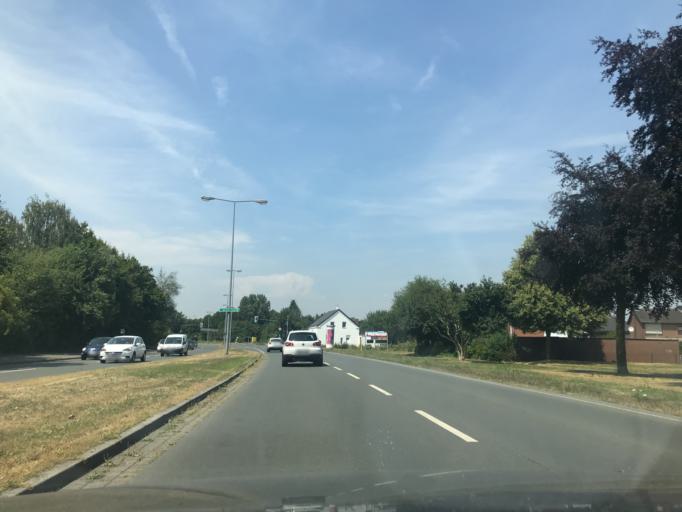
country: DE
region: North Rhine-Westphalia
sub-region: Regierungsbezirk Dusseldorf
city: Wesel
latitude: 51.6776
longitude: 6.6047
